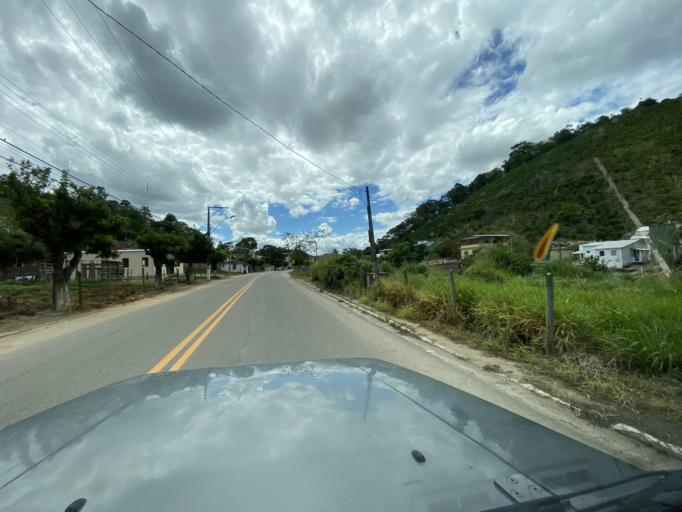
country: BR
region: Espirito Santo
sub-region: Jeronimo Monteiro
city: Jeronimo Monteiro
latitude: -20.7910
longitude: -41.3837
